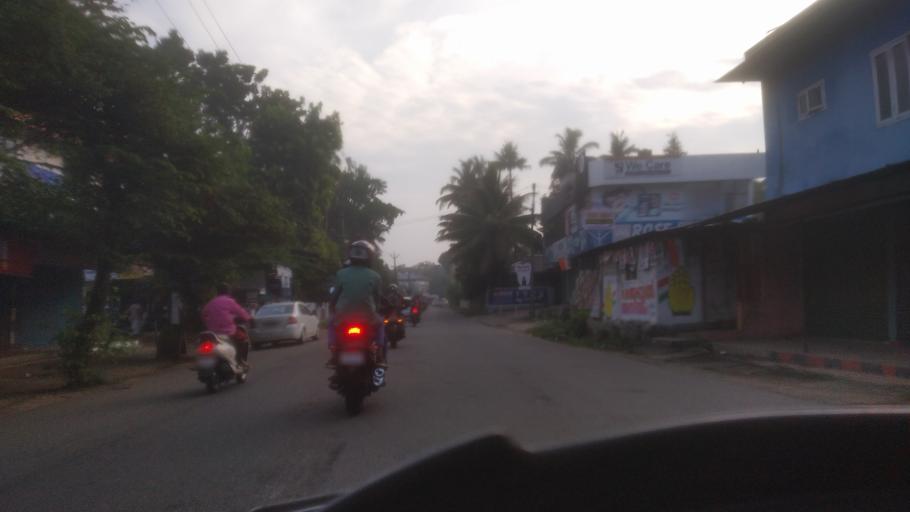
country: IN
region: Kerala
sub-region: Ernakulam
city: Perumpavur
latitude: 10.1194
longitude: 76.4347
